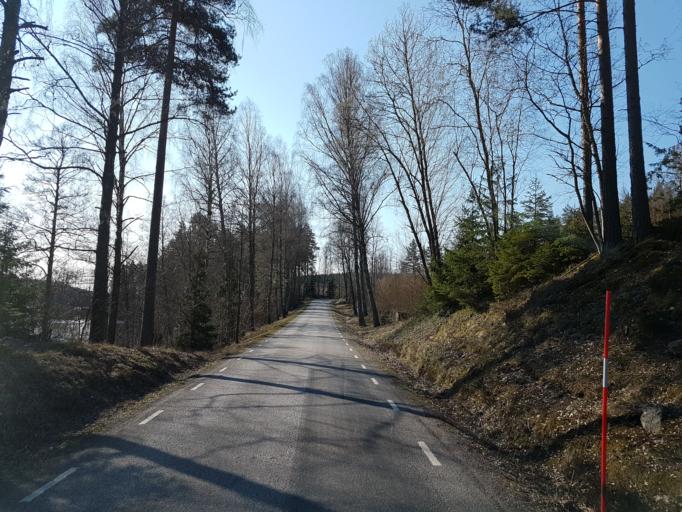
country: SE
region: Kalmar
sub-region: Vasterviks Kommun
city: Overum
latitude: 58.1800
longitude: 16.2806
